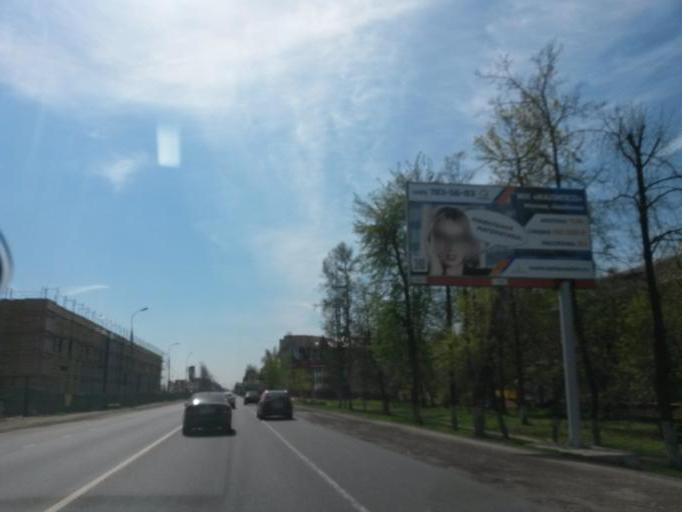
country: RU
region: Moskovskaya
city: Shcherbinka
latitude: 55.5165
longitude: 37.5762
